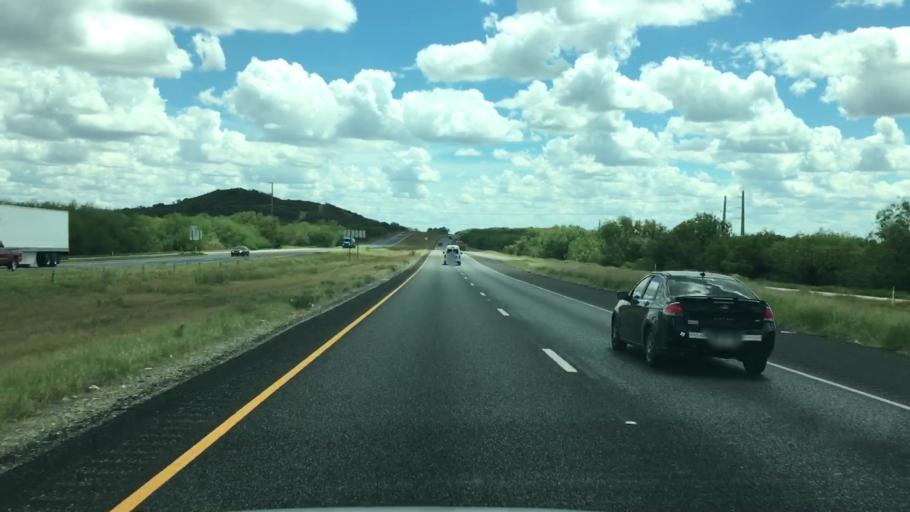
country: US
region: Texas
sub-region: Live Oak County
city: Three Rivers
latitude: 28.7293
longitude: -98.2879
